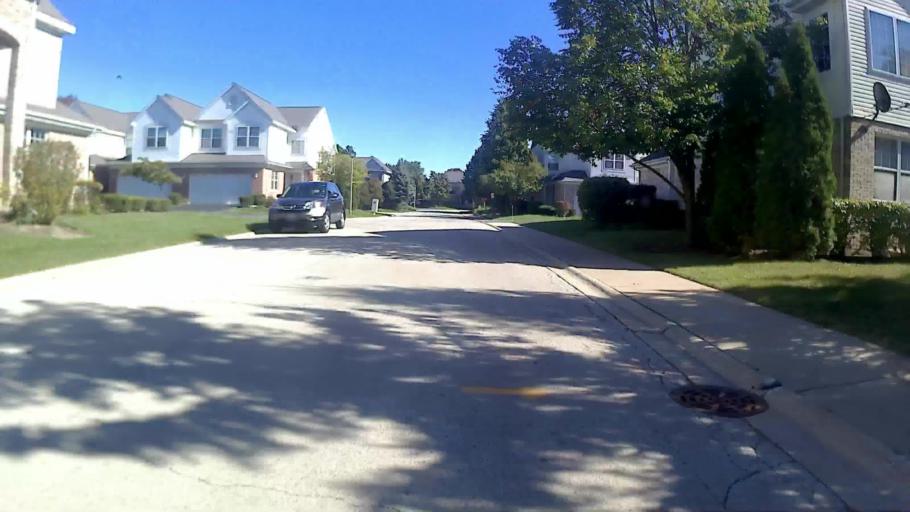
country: US
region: Illinois
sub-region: DuPage County
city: Itasca
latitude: 41.9919
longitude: -88.0161
